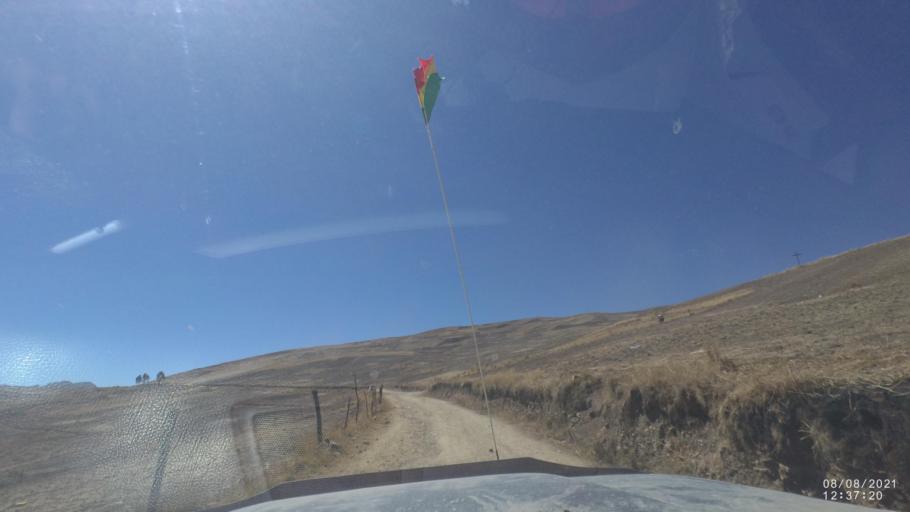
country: BO
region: Cochabamba
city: Colchani
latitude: -16.8381
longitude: -66.6275
